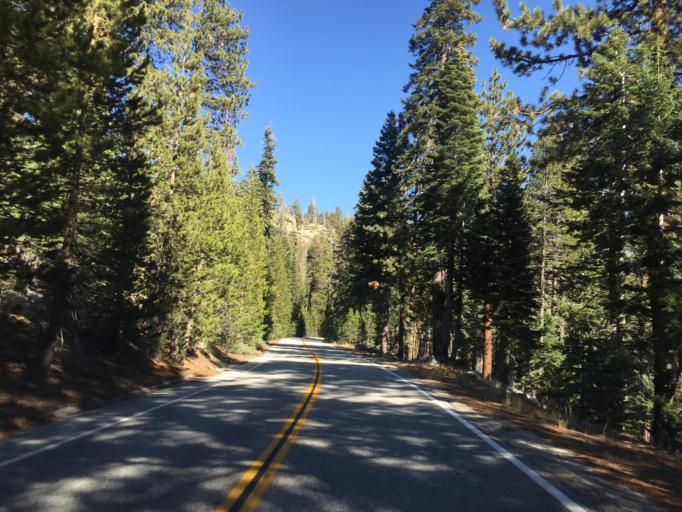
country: US
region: California
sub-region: Mariposa County
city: Yosemite Valley
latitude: 37.8483
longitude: -119.6002
